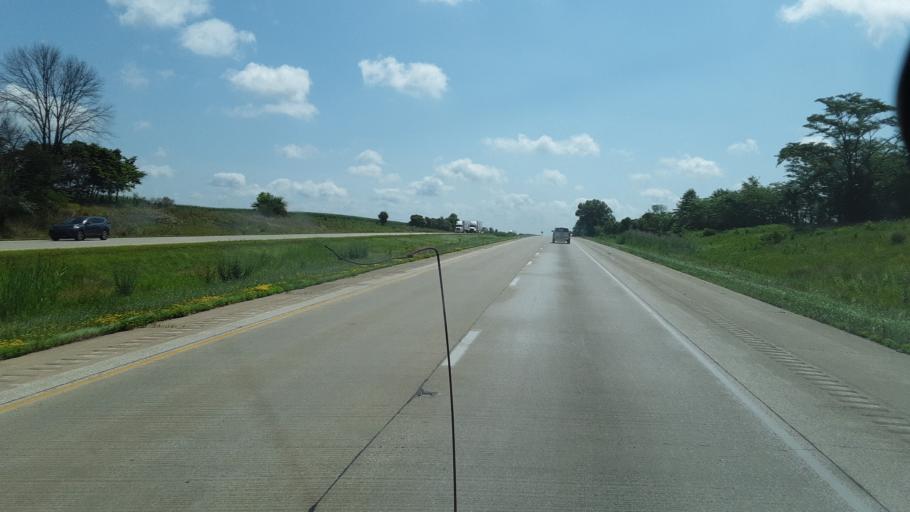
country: US
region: Illinois
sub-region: Clark County
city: Marshall
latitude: 39.4216
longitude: -87.6428
